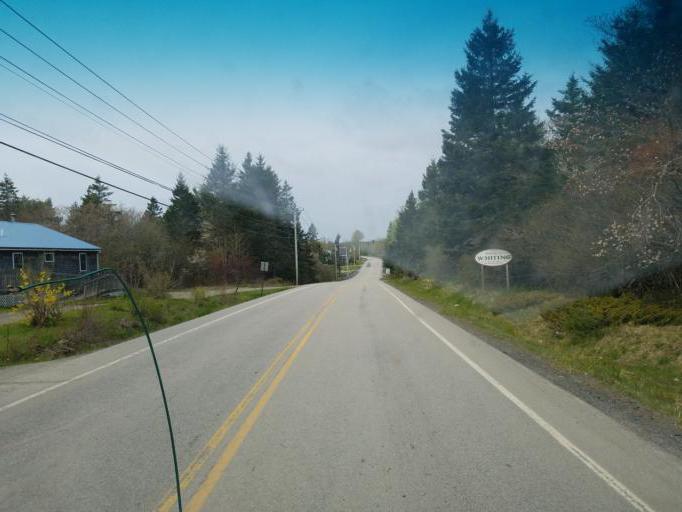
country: US
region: Maine
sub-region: Washington County
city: Eastport
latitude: 44.7900
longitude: -67.1655
